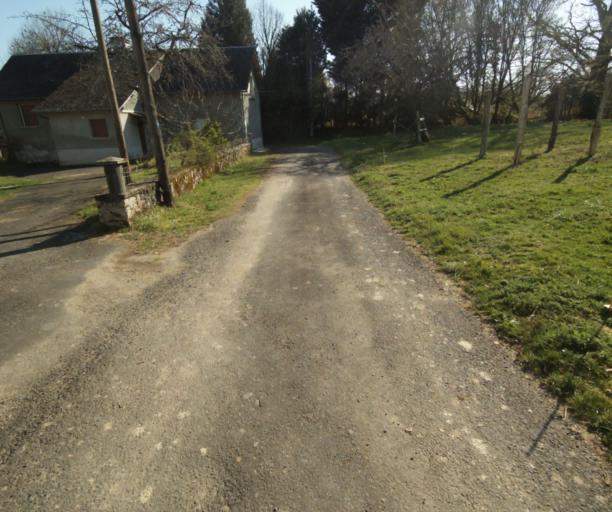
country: FR
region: Limousin
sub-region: Departement de la Correze
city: Saint-Mexant
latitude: 45.3151
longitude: 1.6248
